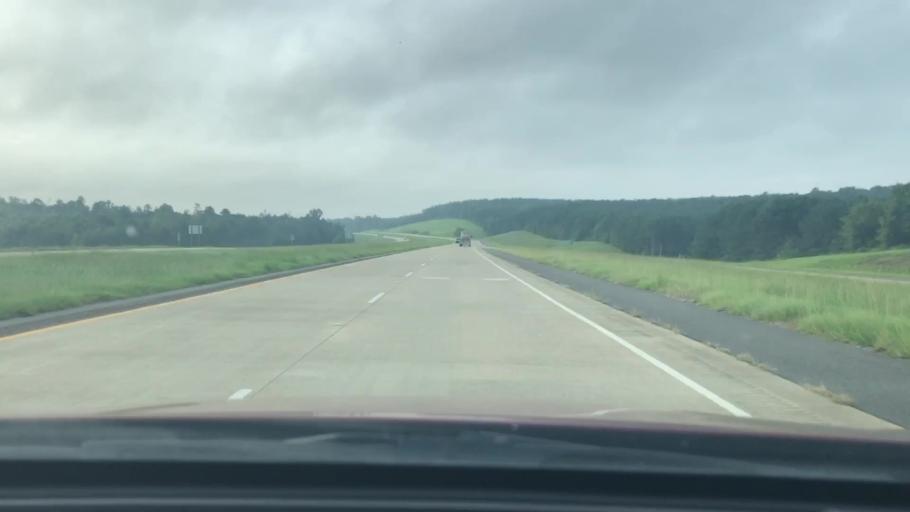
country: US
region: Louisiana
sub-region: Caddo Parish
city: Vivian
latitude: 32.9407
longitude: -93.8977
